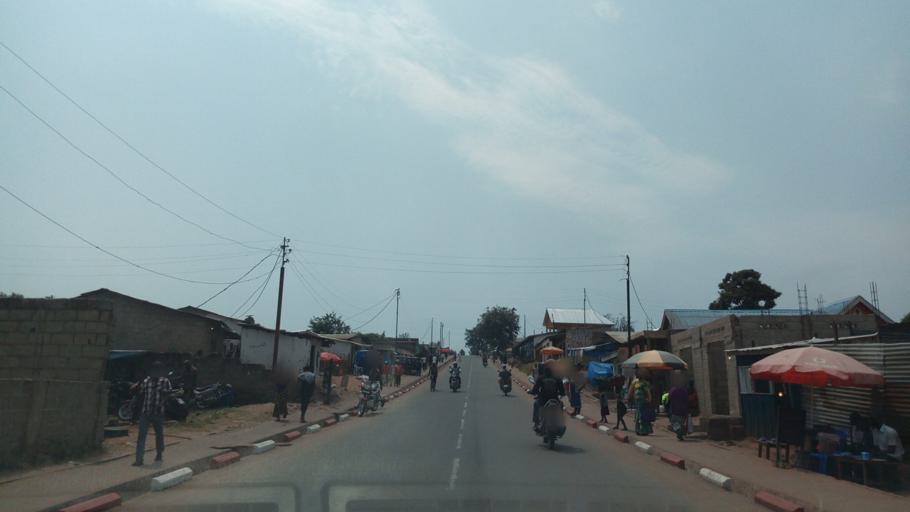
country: CD
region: Katanga
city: Kalemie
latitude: -5.9092
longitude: 29.1959
